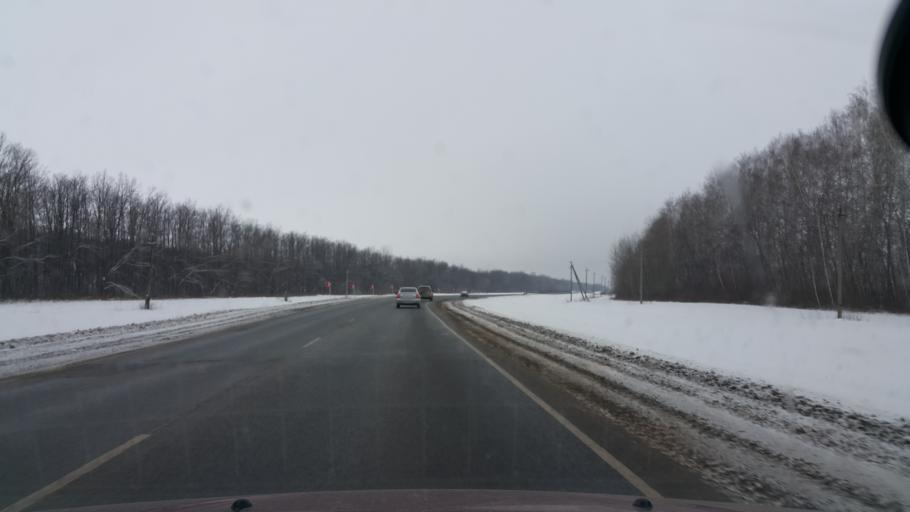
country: RU
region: Tambov
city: Bokino
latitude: 52.5969
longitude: 41.4439
